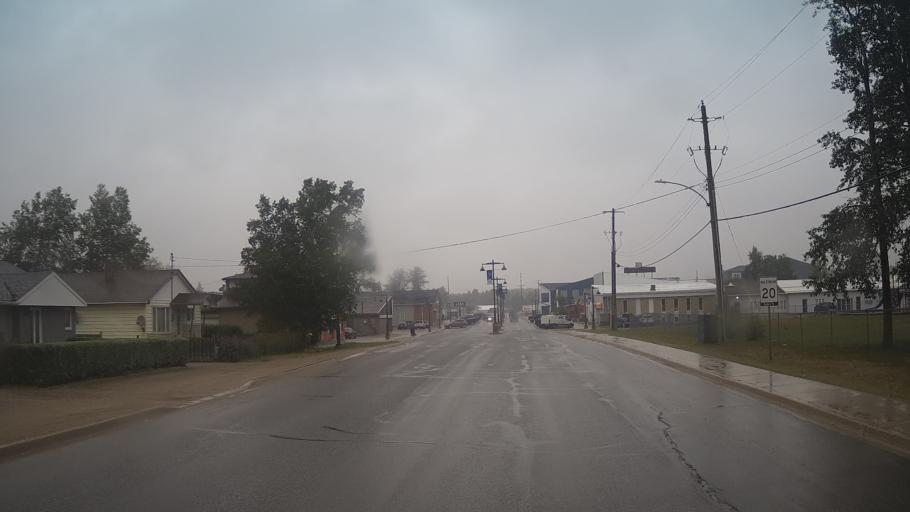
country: CA
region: Ontario
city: Greenstone
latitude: 49.7789
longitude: -86.5353
